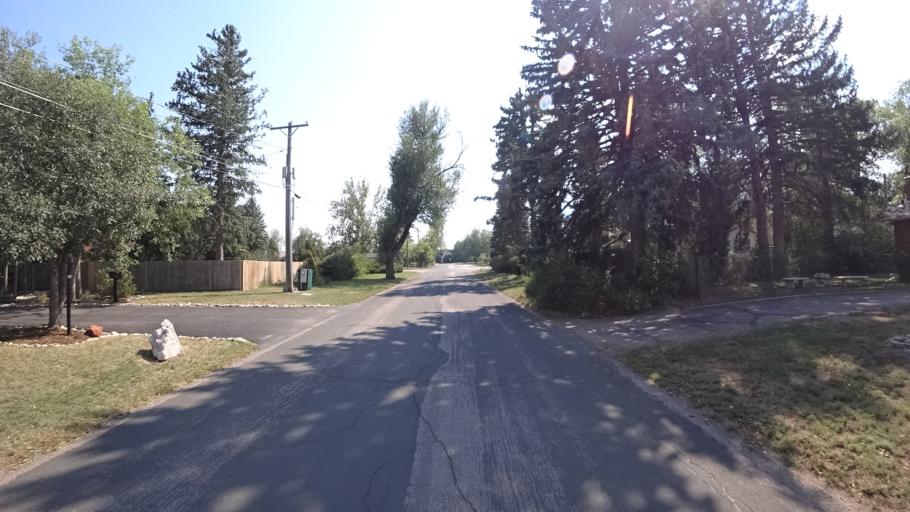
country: US
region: Colorado
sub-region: El Paso County
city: Colorado Springs
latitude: 38.7967
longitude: -104.8338
